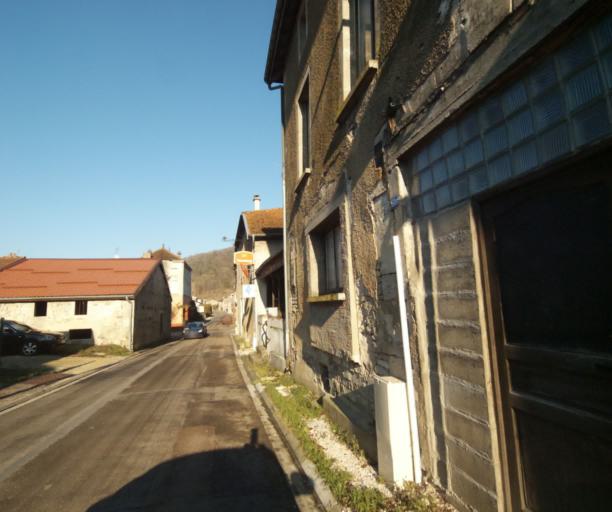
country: FR
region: Champagne-Ardenne
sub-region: Departement de la Haute-Marne
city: Chevillon
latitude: 48.4949
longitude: 5.1914
